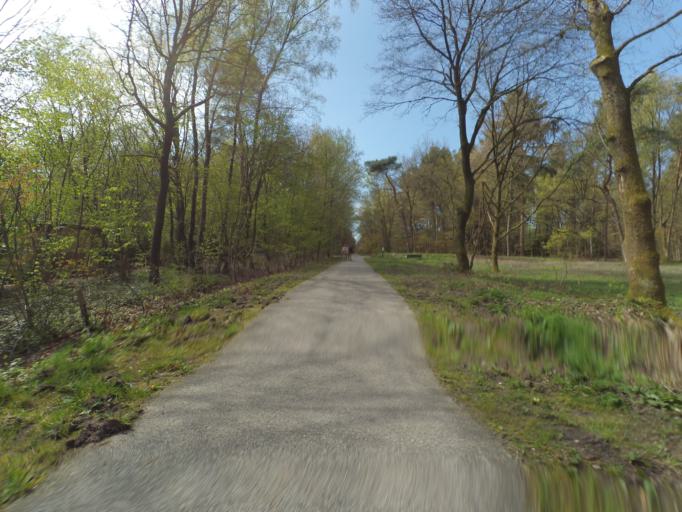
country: NL
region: Gelderland
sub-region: Gemeente Epe
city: Epe
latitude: 52.3700
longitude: 6.0030
